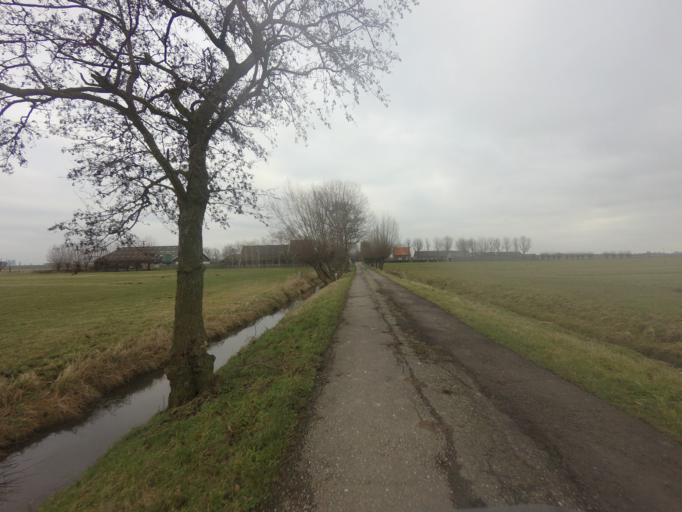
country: NL
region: Utrecht
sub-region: Gemeente IJsselstein
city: IJsselstein
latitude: 52.0583
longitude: 5.0510
